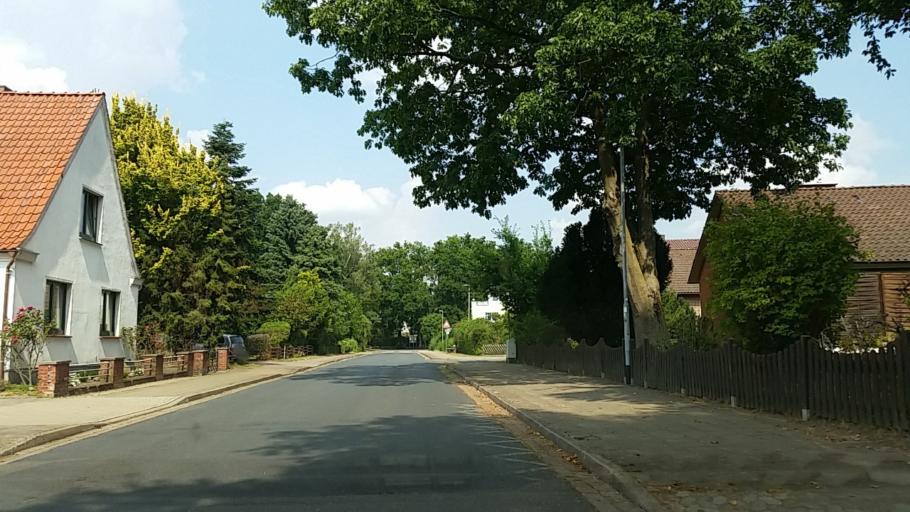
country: DE
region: Lower Saxony
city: Schneverdingen
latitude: 53.1263
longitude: 9.7855
